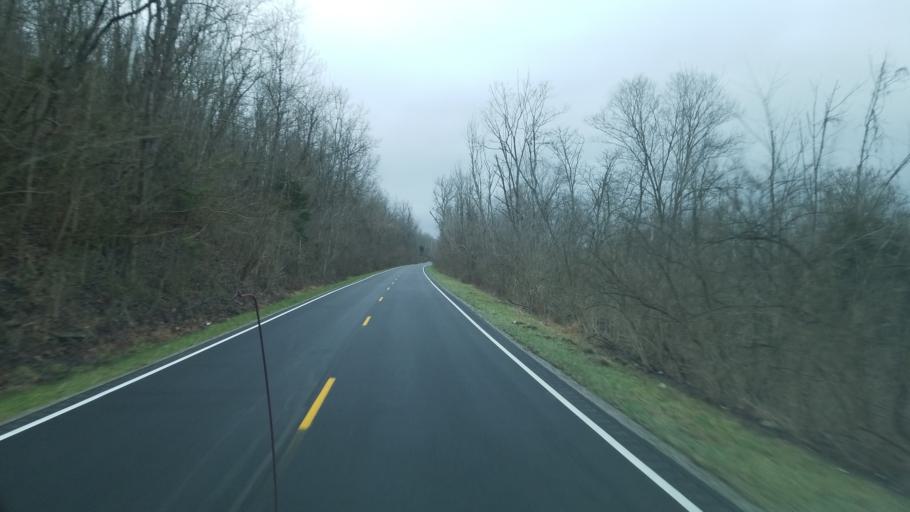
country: US
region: Ohio
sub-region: Brown County
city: Ripley
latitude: 38.7619
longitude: -83.9177
